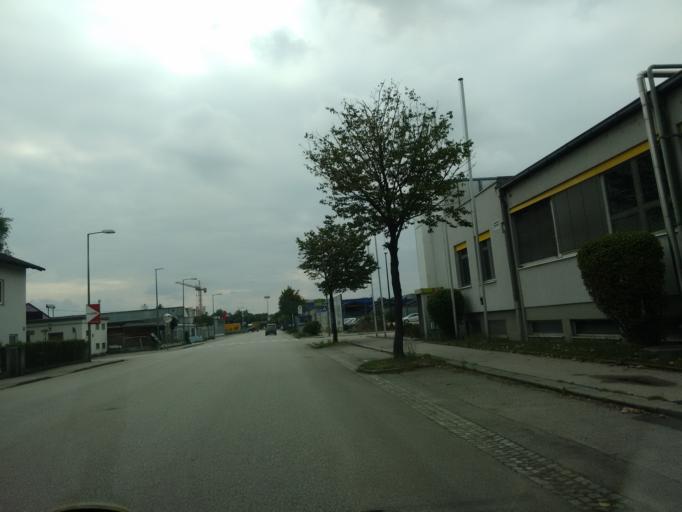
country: AT
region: Upper Austria
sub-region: Wels Stadt
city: Wels
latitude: 48.1608
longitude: 14.0502
